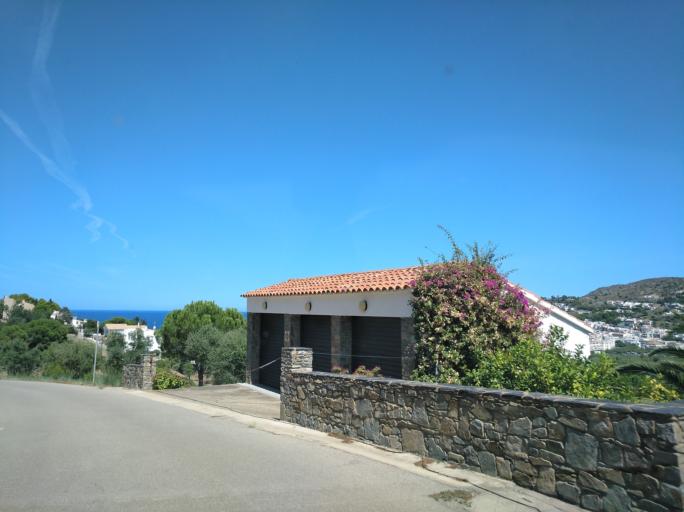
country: ES
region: Catalonia
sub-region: Provincia de Girona
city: Llanca
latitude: 42.3307
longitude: 3.1950
